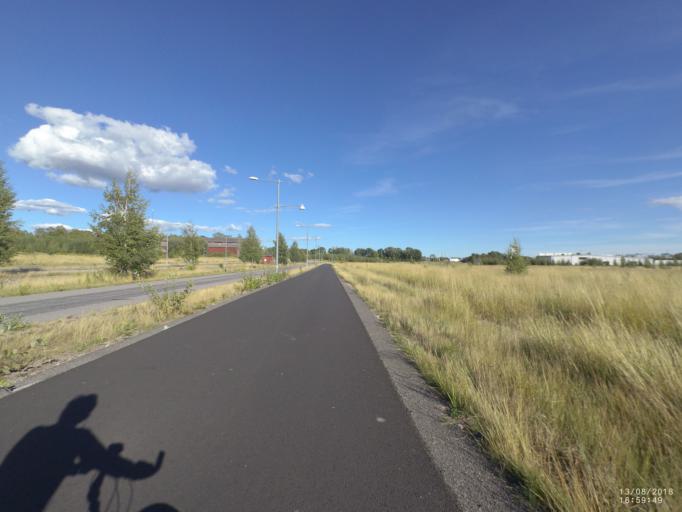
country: SE
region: Soedermanland
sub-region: Nykopings Kommun
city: Nykoping
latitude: 58.7545
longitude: 16.9740
